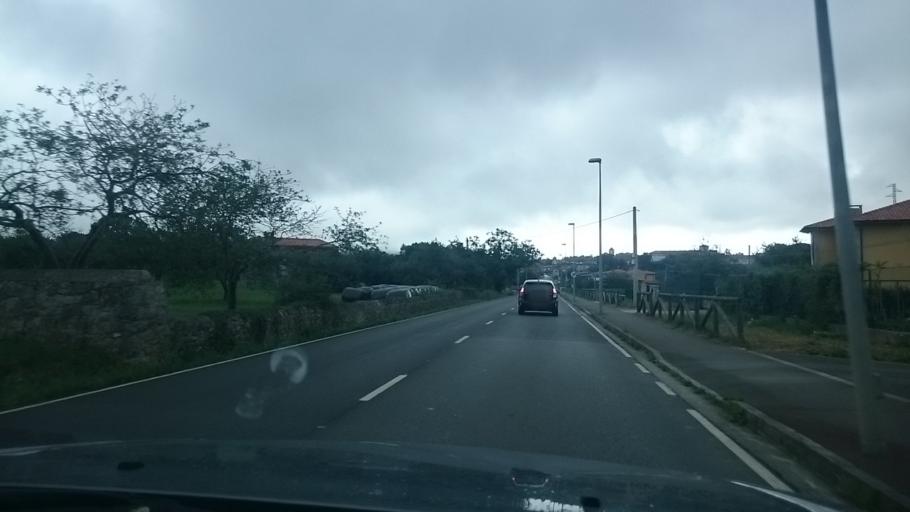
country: ES
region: Asturias
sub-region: Province of Asturias
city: Carrena
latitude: 43.4191
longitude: -4.8710
